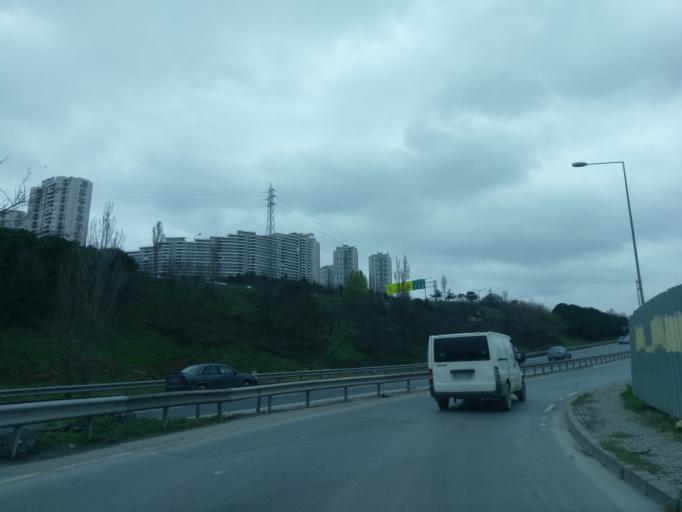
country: TR
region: Istanbul
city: Basaksehir
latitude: 41.0606
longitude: 28.7720
